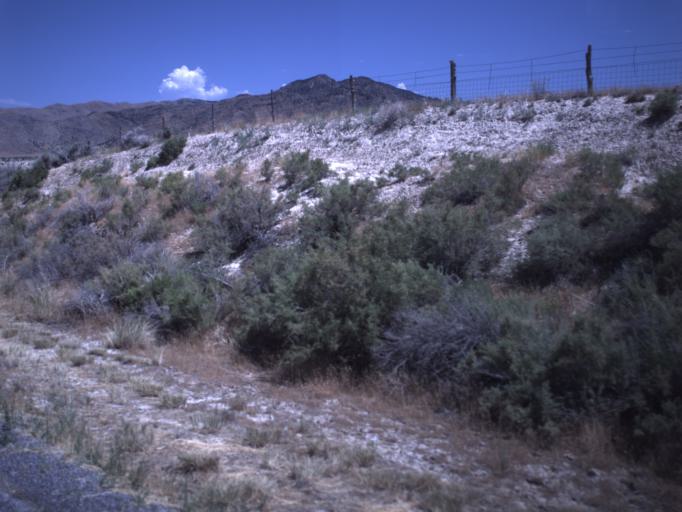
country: US
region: Utah
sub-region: Millard County
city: Delta
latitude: 39.5153
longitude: -112.2727
